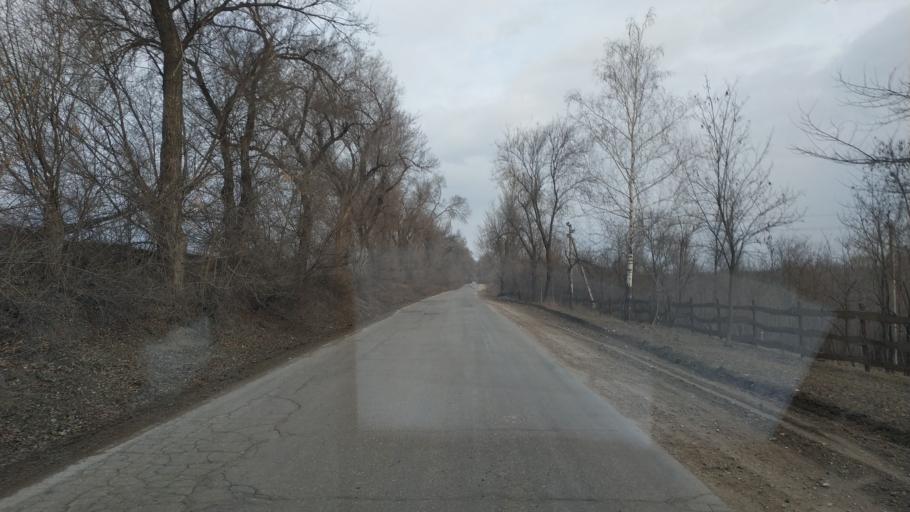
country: MD
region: Chisinau
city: Singera
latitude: 46.9294
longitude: 29.0483
